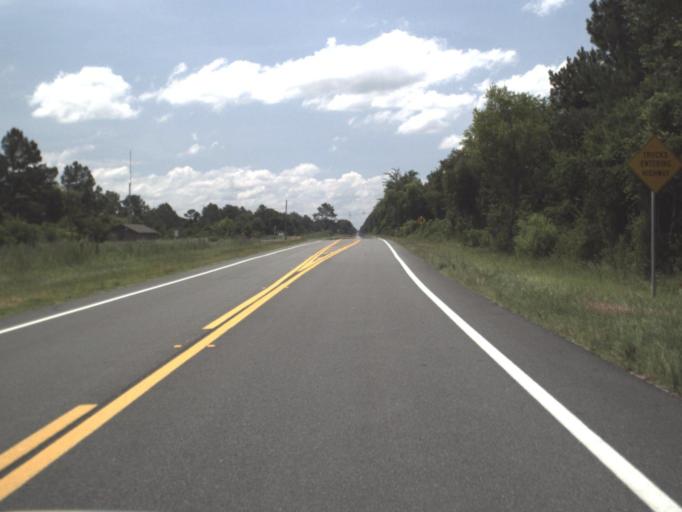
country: US
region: Florida
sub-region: Hamilton County
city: Jasper
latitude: 30.4377
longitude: -82.8735
